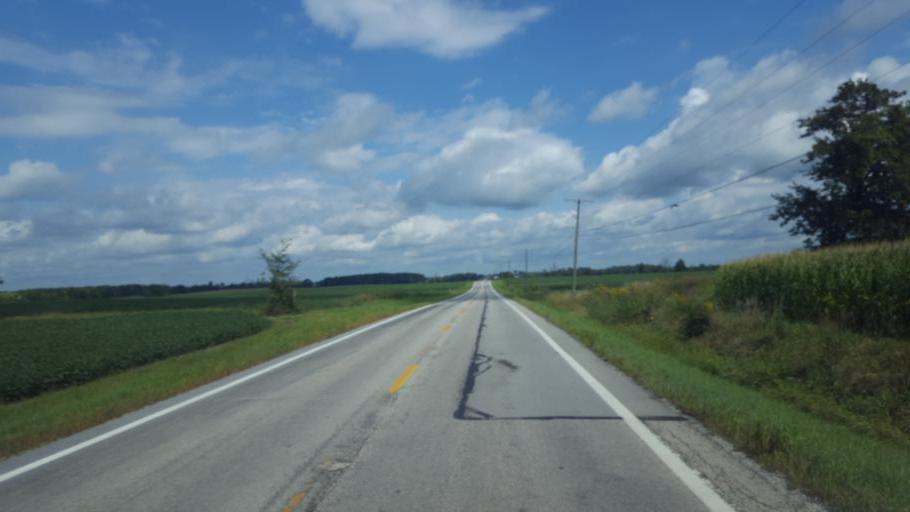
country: US
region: Ohio
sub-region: Seneca County
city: Tiffin
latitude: 41.0880
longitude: -83.0152
